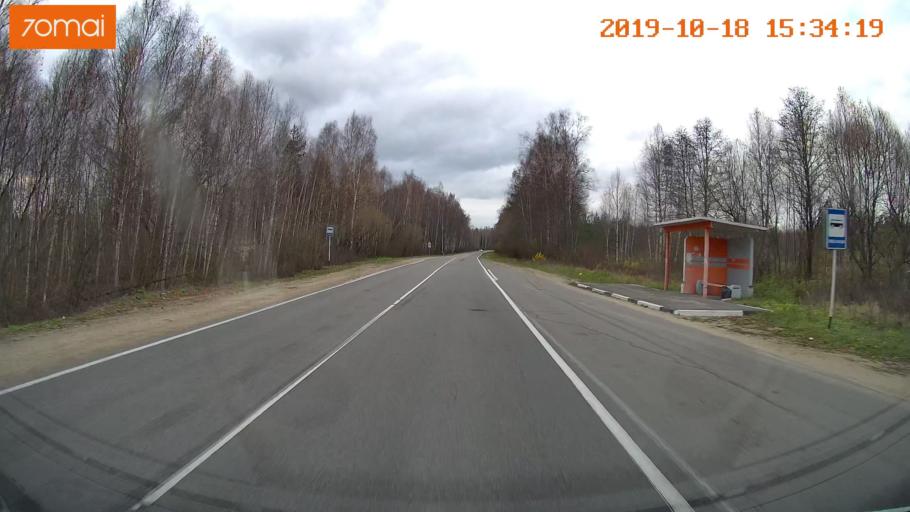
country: RU
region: Vladimir
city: Anopino
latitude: 55.8532
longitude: 40.6442
